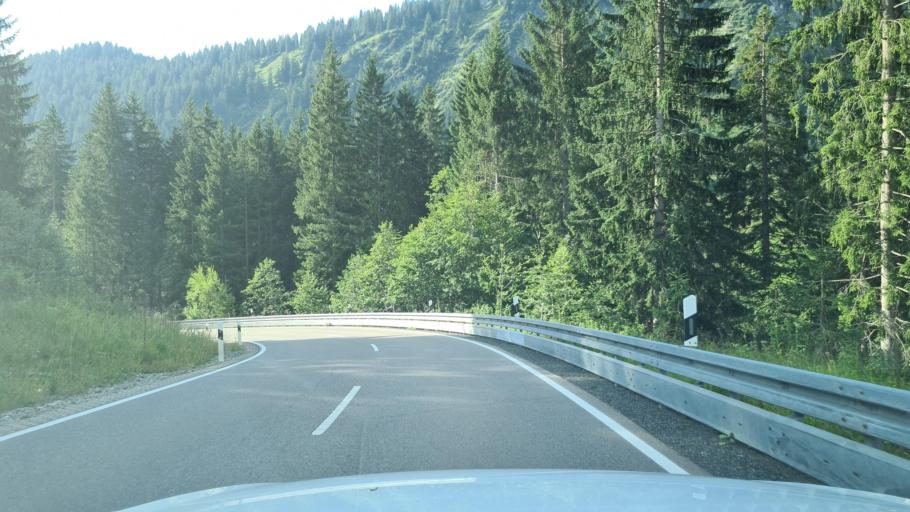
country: DE
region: Bavaria
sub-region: Swabia
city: Obermaiselstein
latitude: 47.4336
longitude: 10.1908
